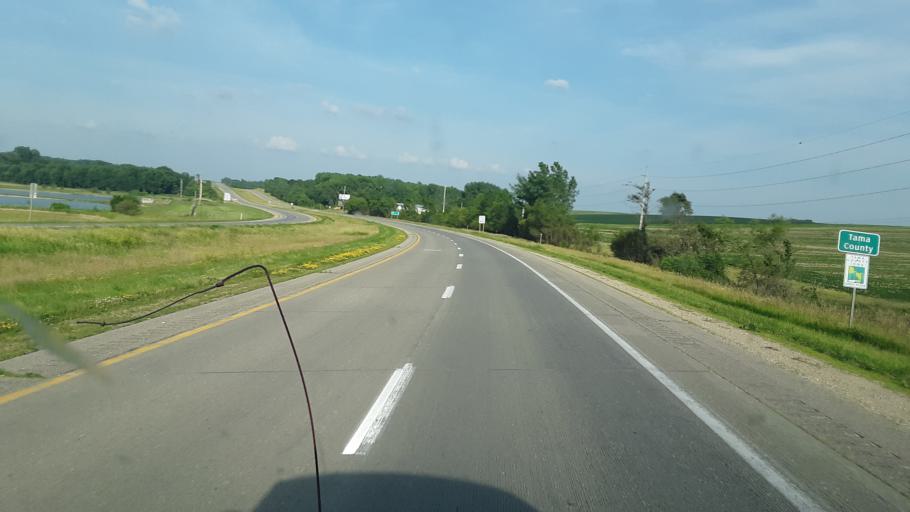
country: US
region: Iowa
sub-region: Marshall County
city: Marshalltown
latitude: 42.0069
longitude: -92.7664
